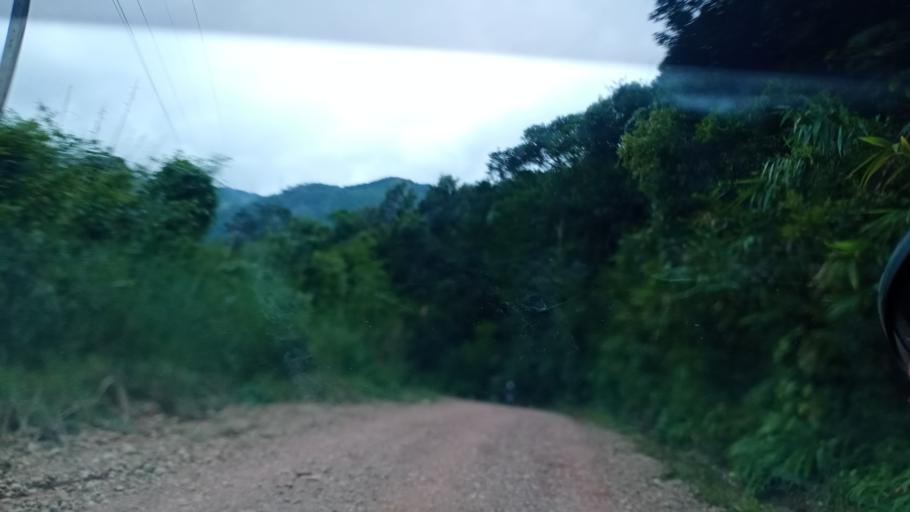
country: TH
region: Changwat Bueng Kan
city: Pak Khat
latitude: 18.7231
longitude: 103.2466
